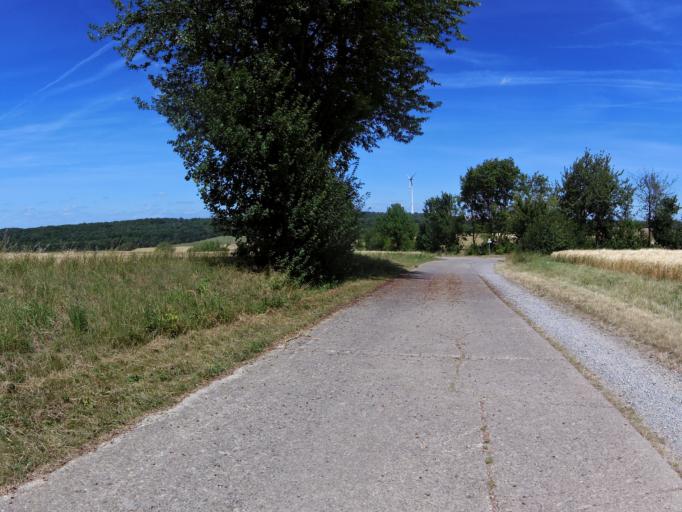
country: DE
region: Bavaria
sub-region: Regierungsbezirk Unterfranken
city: Hettstadt
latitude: 49.8101
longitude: 9.8217
